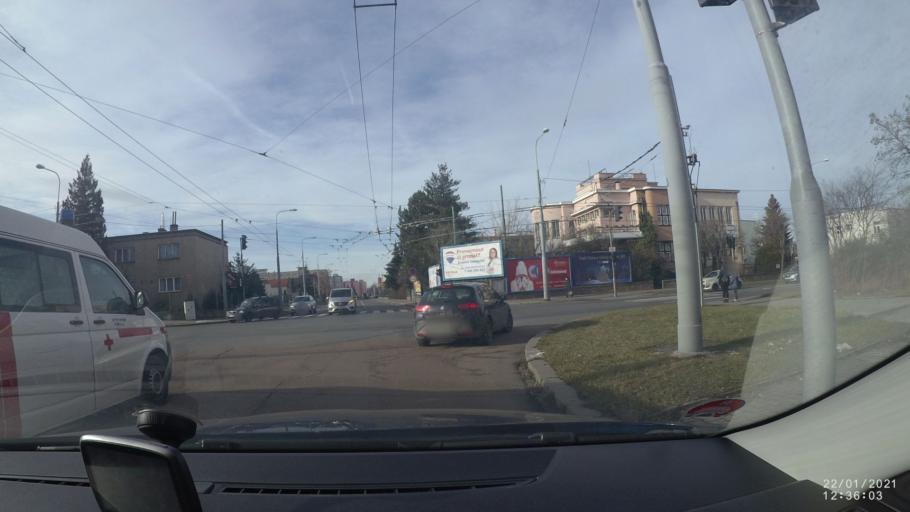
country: CZ
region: Plzensky
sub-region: Okres Plzen-Mesto
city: Pilsen
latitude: 49.7498
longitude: 13.4141
